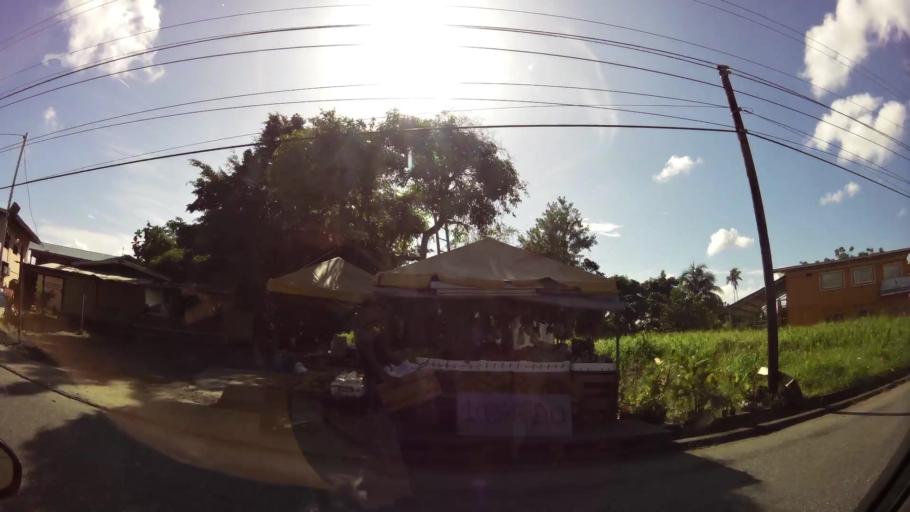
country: TT
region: Chaguanas
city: Chaguanas
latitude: 10.5317
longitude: -61.4029
